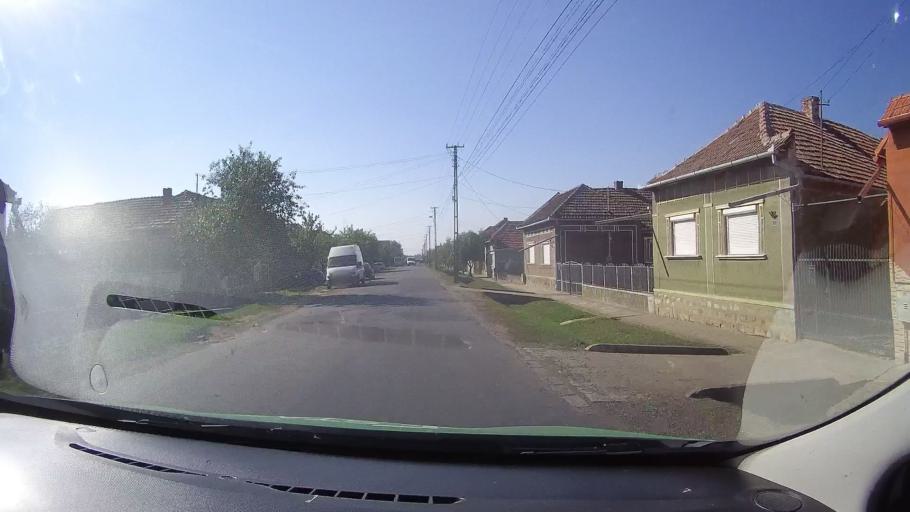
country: RO
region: Satu Mare
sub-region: Comuna Capleni
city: Capleni
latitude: 47.7012
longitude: 22.4912
